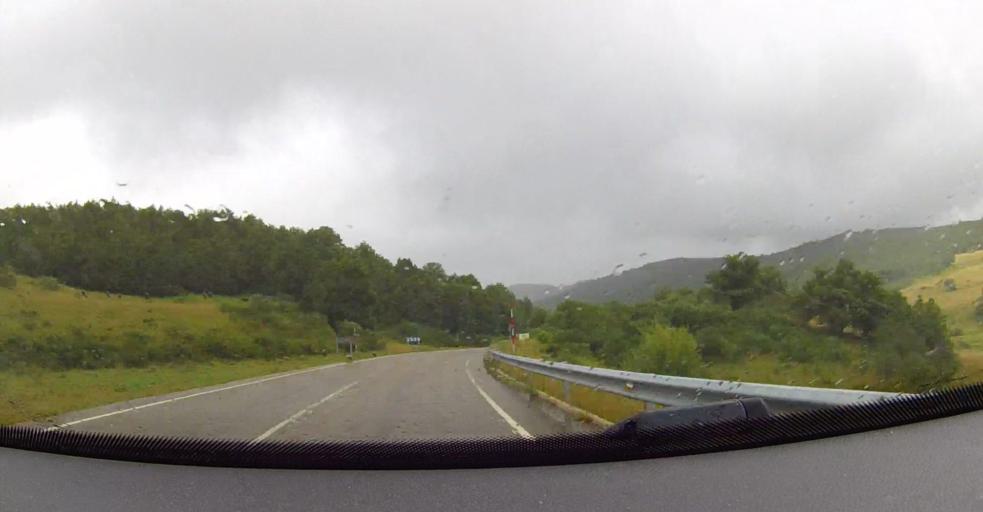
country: ES
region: Castille and Leon
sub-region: Provincia de Leon
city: Marana
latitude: 43.0716
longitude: -5.1939
